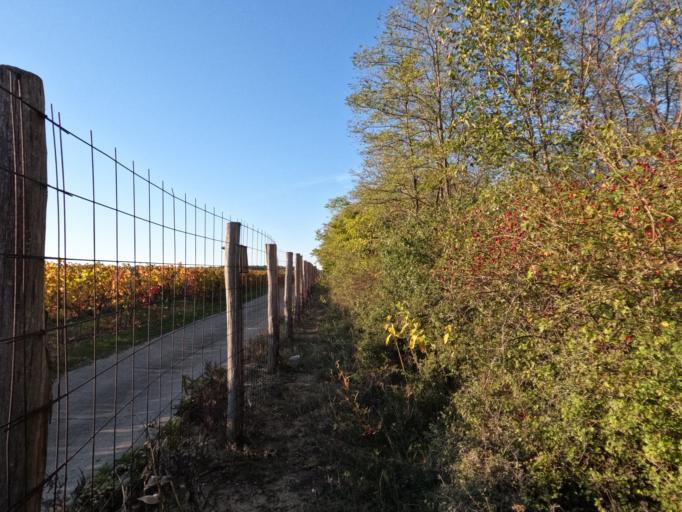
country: HU
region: Tolna
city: Szekszard
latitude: 46.3084
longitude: 18.6595
